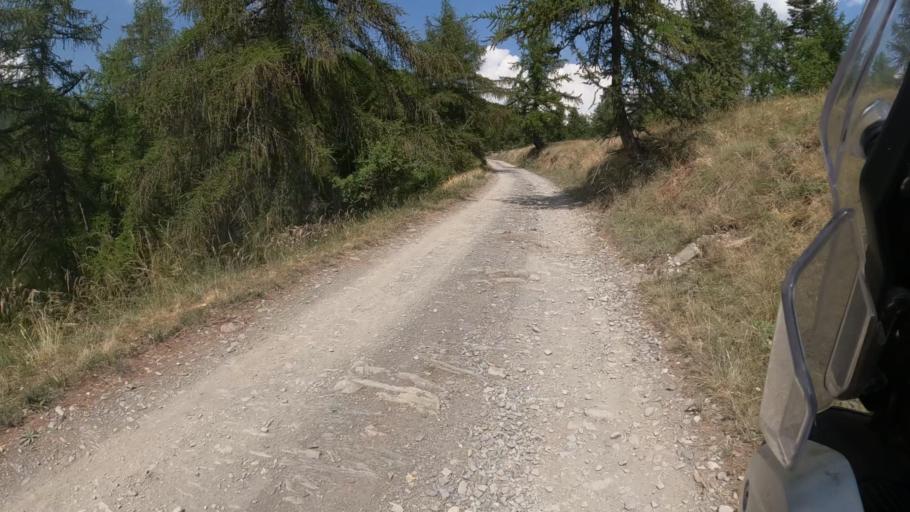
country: IT
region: Piedmont
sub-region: Provincia di Cuneo
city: Briga Alta
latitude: 44.0301
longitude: 7.6717
